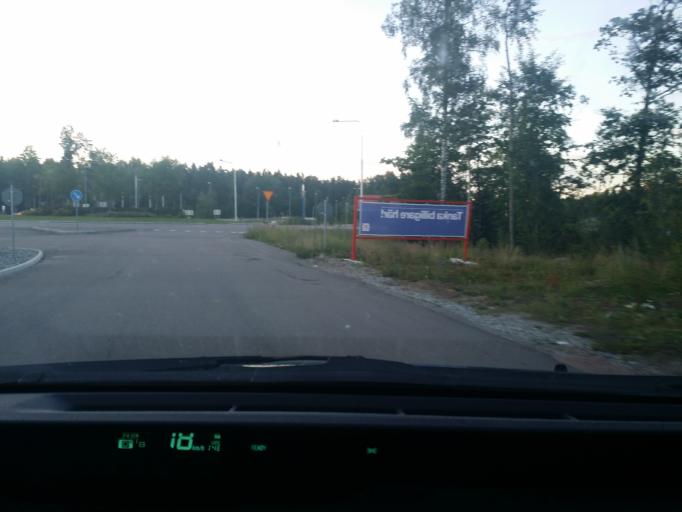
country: SE
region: Vaestmanland
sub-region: Vasteras
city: Vasteras
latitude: 59.6360
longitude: 16.5464
